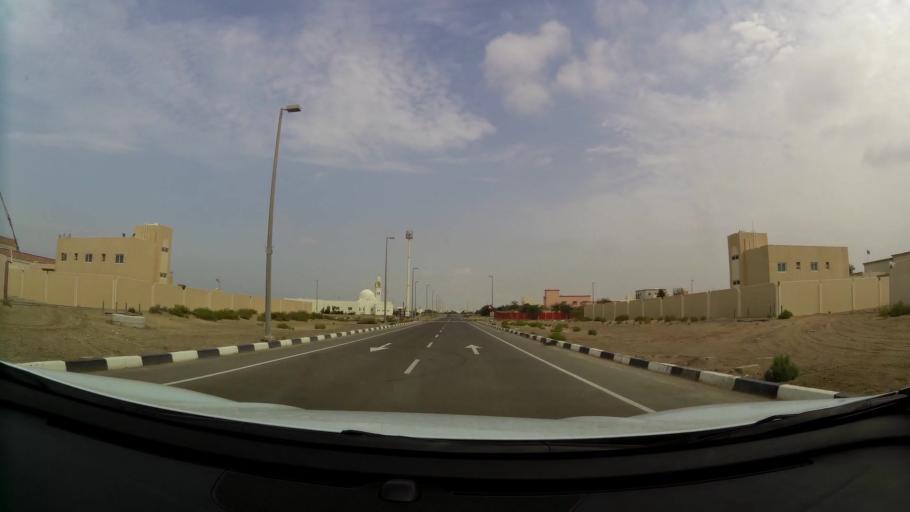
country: AE
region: Abu Dhabi
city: Abu Dhabi
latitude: 24.6343
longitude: 54.6709
